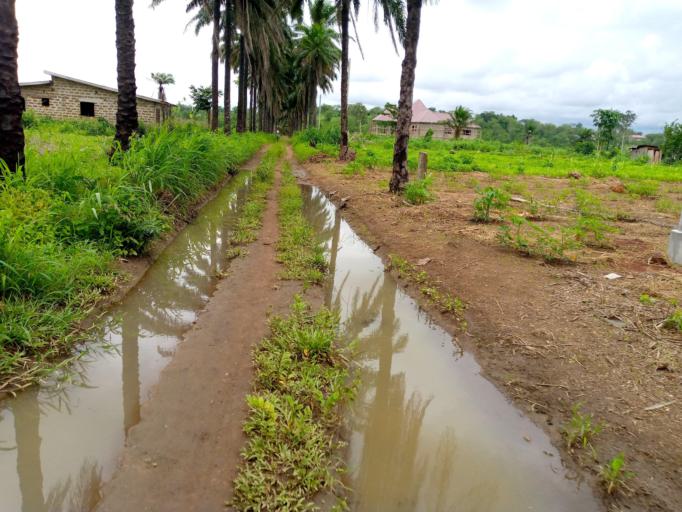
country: SL
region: Southern Province
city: Moyamba
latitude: 8.1515
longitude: -12.4431
